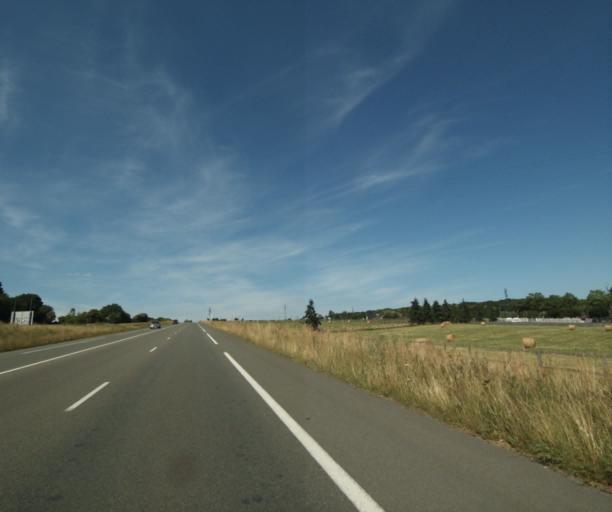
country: FR
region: Pays de la Loire
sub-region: Departement de la Mayenne
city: Montigne-le-Brillant
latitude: 48.0375
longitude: -0.8031
